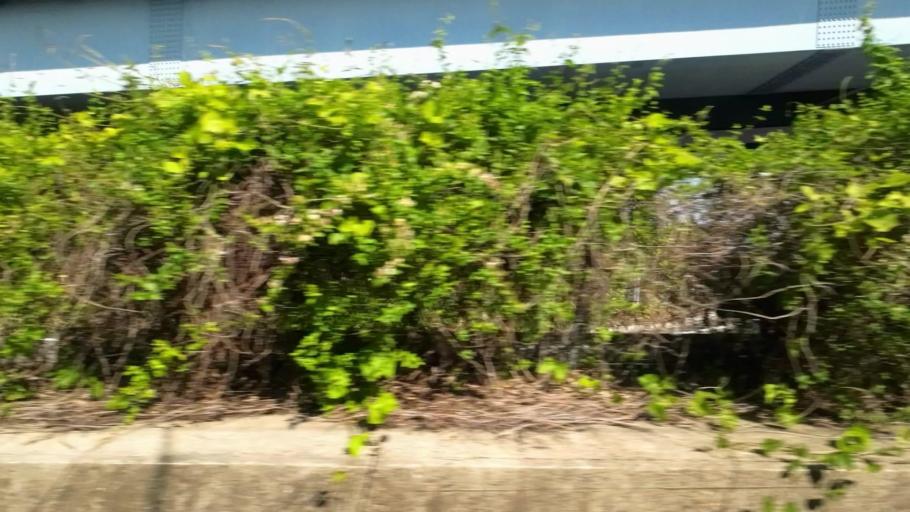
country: JP
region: Kagawa
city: Tadotsu
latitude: 34.2352
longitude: 133.7011
